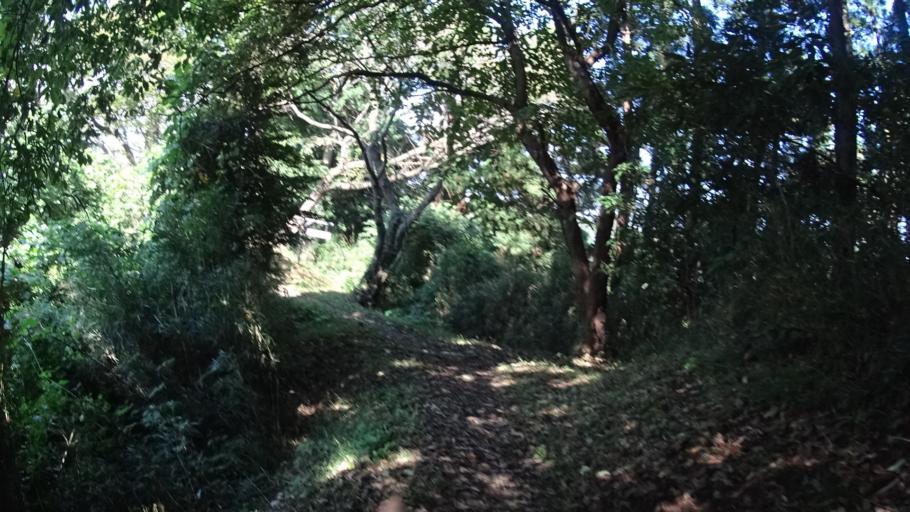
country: JP
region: Kanagawa
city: Kamakura
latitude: 35.3600
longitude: 139.5850
